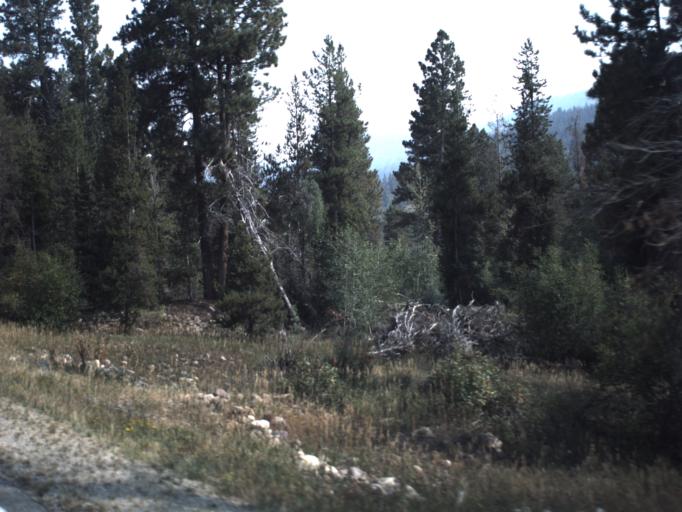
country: US
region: Utah
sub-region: Summit County
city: Kamas
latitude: 40.6299
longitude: -111.1779
